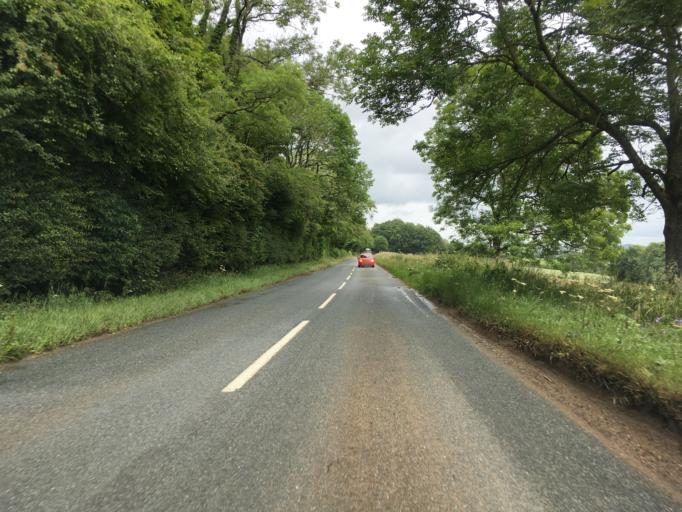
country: GB
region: England
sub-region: Gloucestershire
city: Chipping Campden
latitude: 52.0487
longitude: -1.8047
